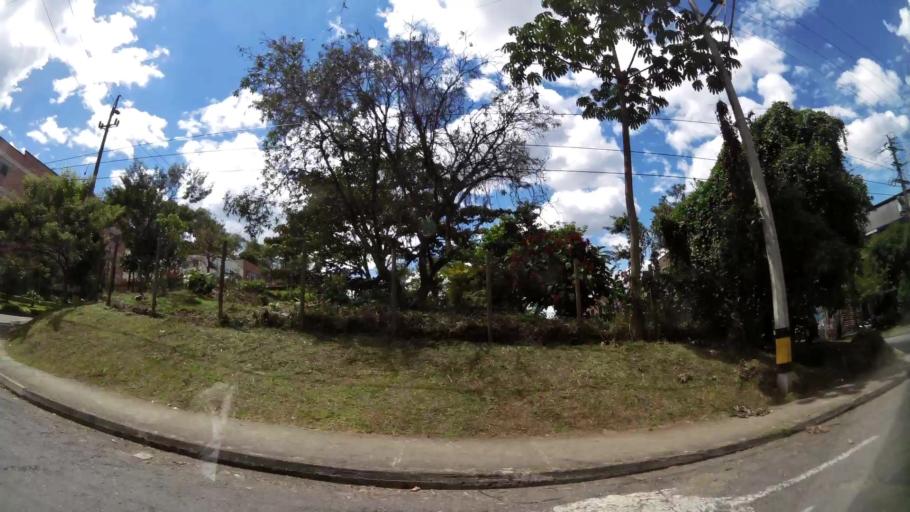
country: CO
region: Antioquia
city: Sabaneta
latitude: 6.1481
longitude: -75.6270
